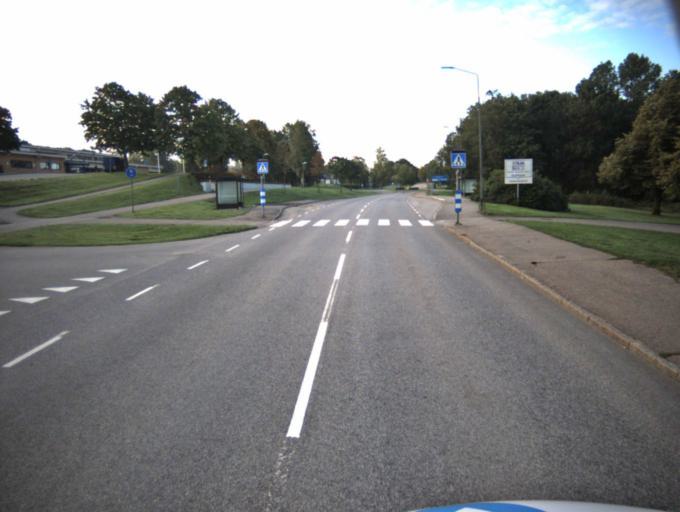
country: SE
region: Vaestra Goetaland
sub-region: Ulricehamns Kommun
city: Ulricehamn
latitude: 57.7900
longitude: 13.4264
